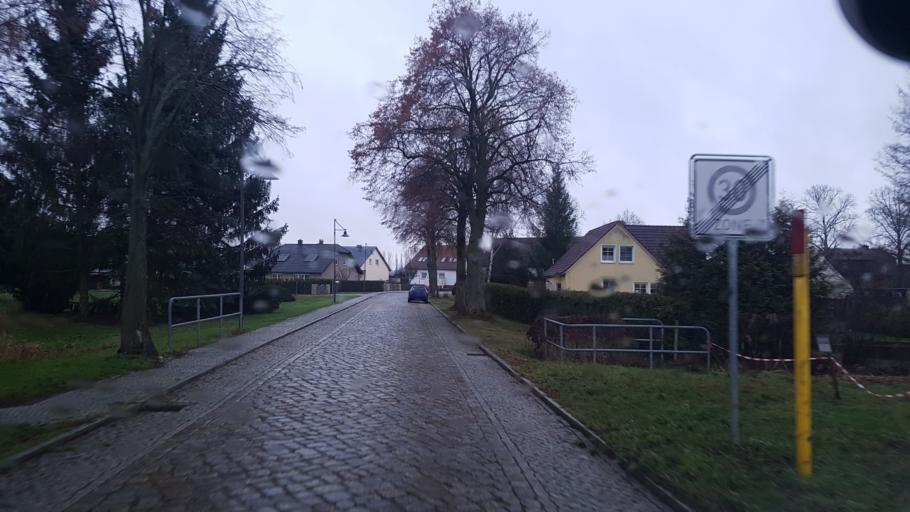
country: DE
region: Brandenburg
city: Ludwigsfelde
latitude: 52.3176
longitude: 13.1938
